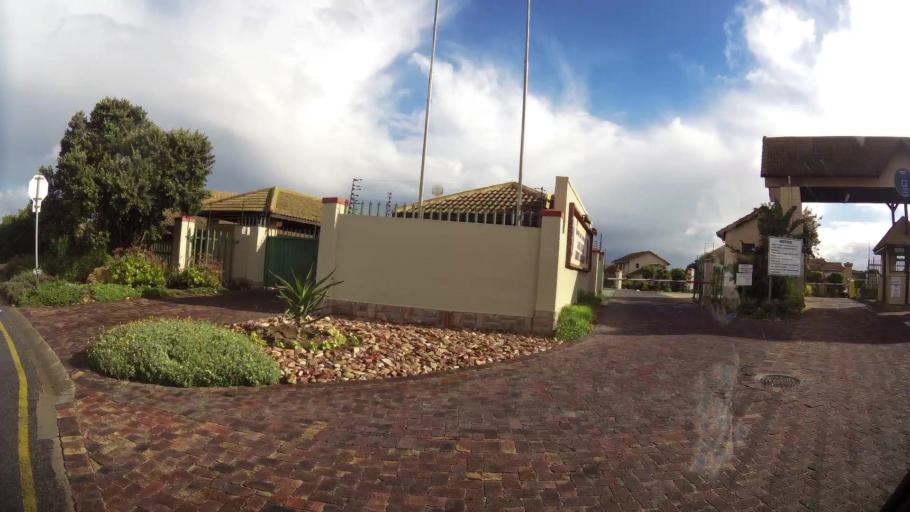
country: ZA
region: Western Cape
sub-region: Eden District Municipality
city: Mossel Bay
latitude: -34.1917
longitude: 22.1374
